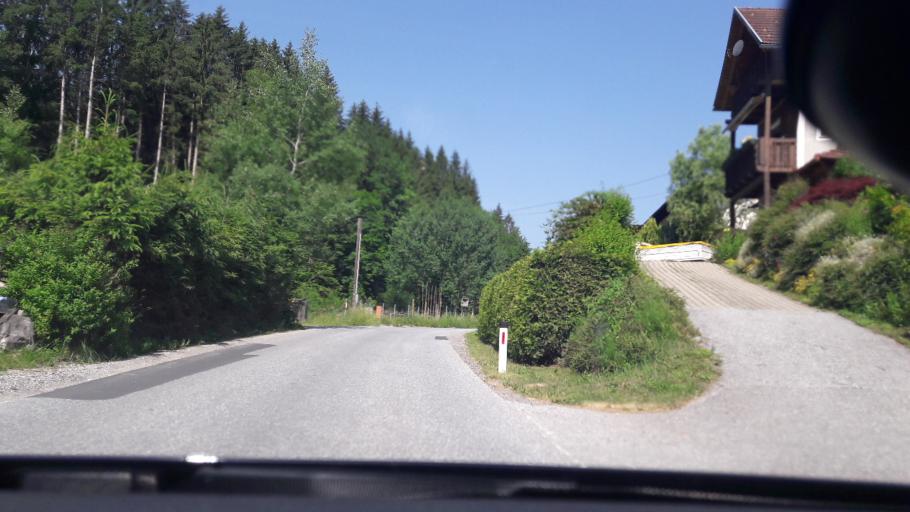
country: AT
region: Styria
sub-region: Politischer Bezirk Voitsberg
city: Sodingberg
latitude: 47.1083
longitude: 15.1678
